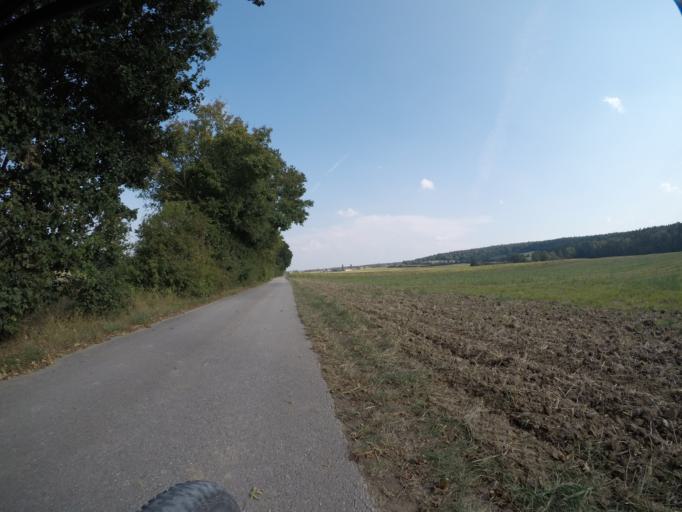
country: AT
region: Lower Austria
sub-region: Politischer Bezirk Baden
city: Hirtenberg
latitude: 47.9643
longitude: 16.1522
